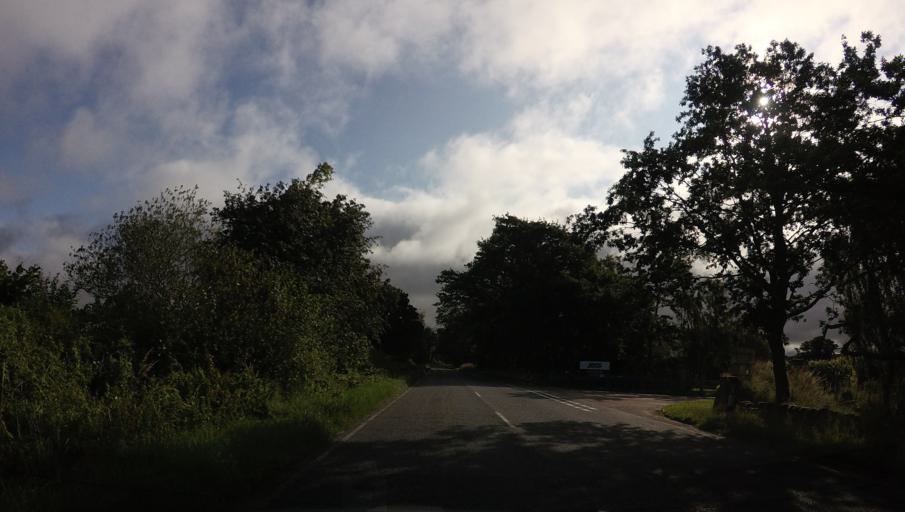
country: GB
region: Scotland
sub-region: Aberdeenshire
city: Banchory
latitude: 57.0648
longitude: -2.3854
